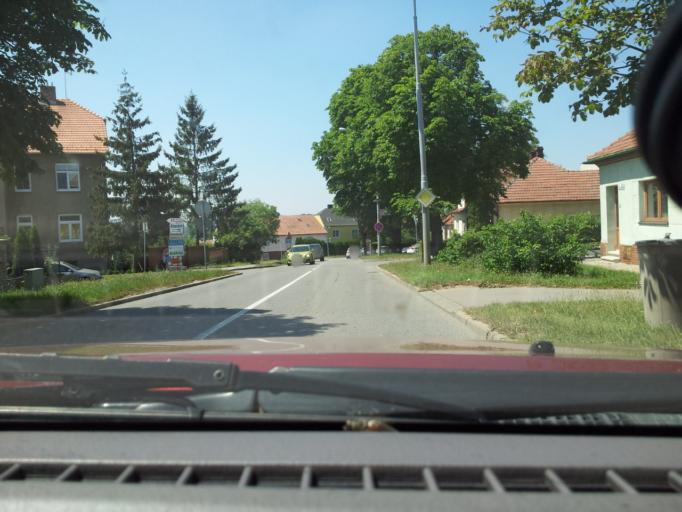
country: CZ
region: South Moravian
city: Modrice
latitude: 49.1546
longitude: 16.6511
